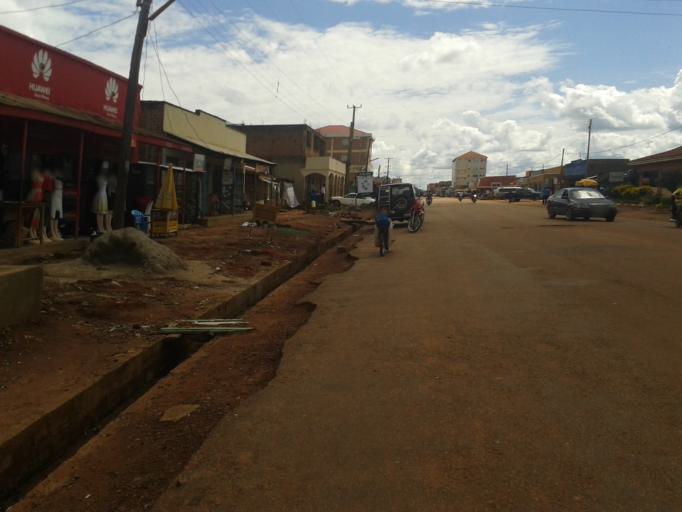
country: UG
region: Northern Region
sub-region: Gulu District
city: Gulu
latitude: 2.7702
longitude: 32.3035
